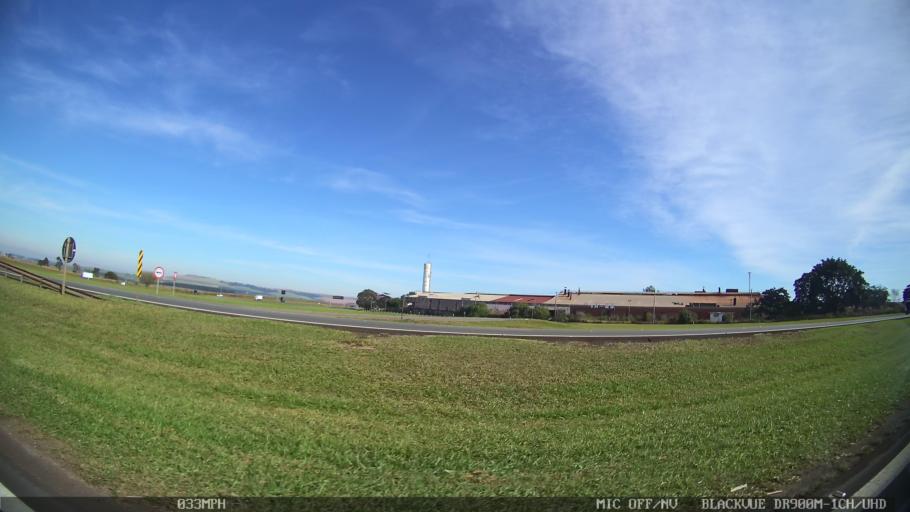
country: BR
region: Sao Paulo
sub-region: Cordeiropolis
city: Cordeiropolis
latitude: -22.5009
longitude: -47.3994
